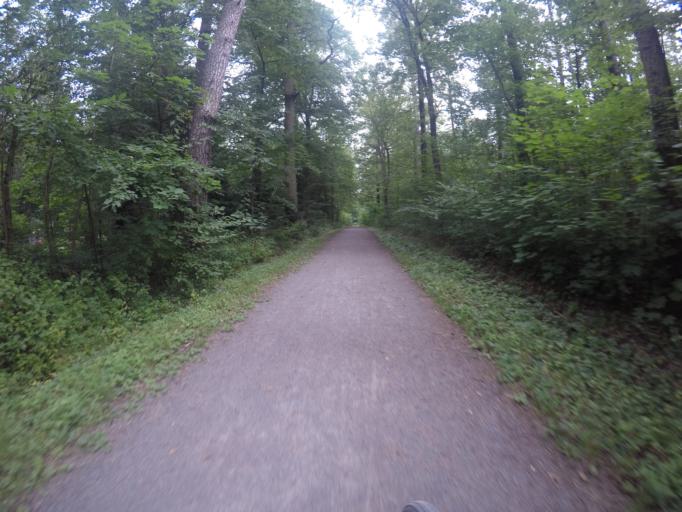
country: DE
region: Baden-Wuerttemberg
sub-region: Regierungsbezirk Stuttgart
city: Stuttgart
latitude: 48.7485
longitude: 9.1444
